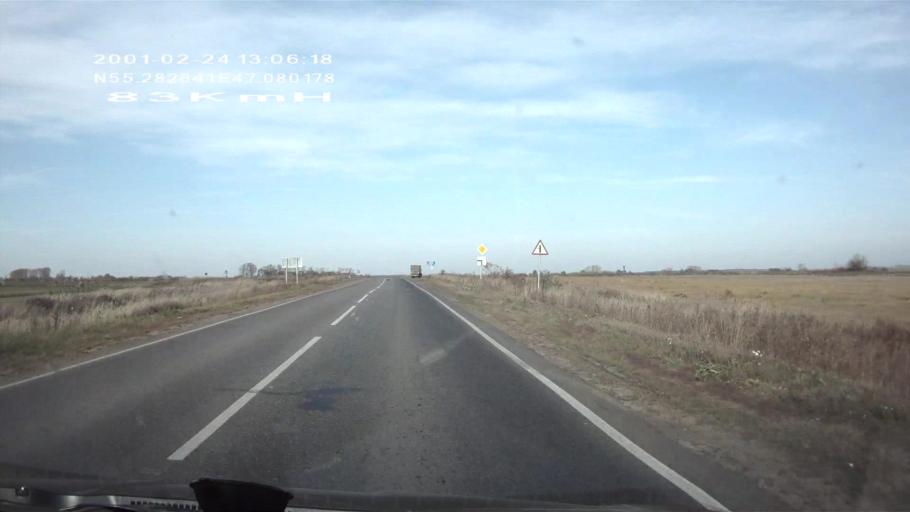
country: RU
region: Chuvashia
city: Ibresi
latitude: 55.2827
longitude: 47.0802
